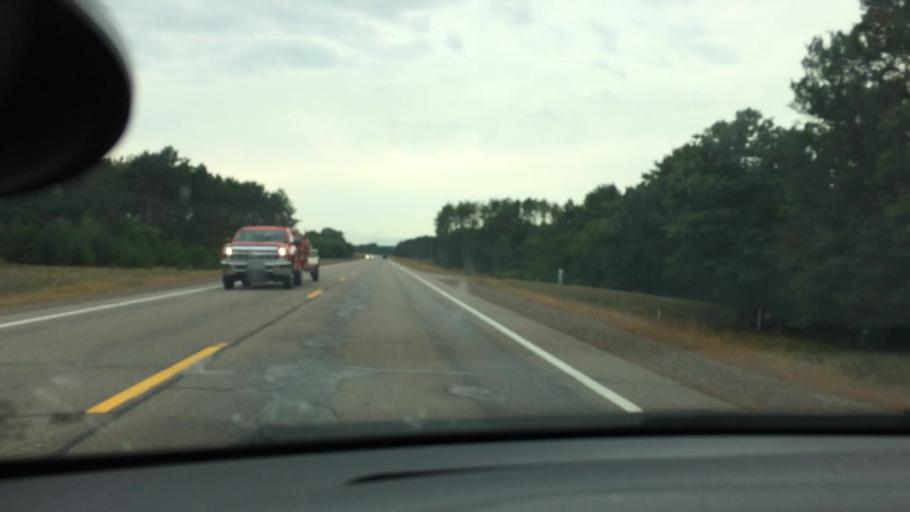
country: US
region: Wisconsin
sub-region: Eau Claire County
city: Augusta
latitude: 44.5825
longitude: -91.0869
